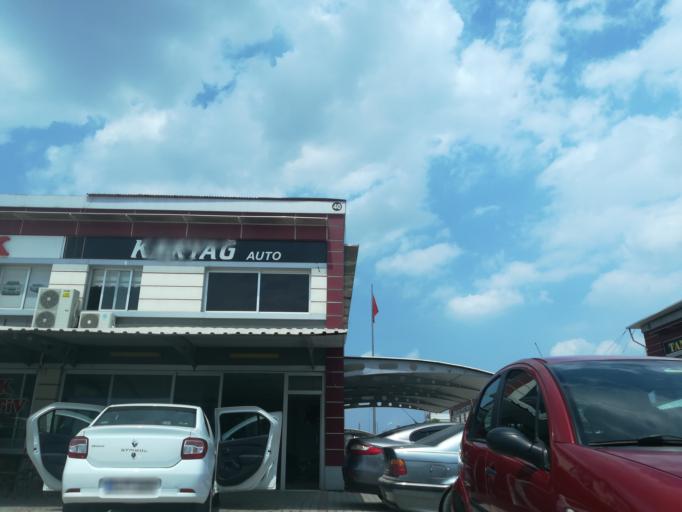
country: TR
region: Adana
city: Seyhan
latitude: 37.0015
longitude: 35.2446
